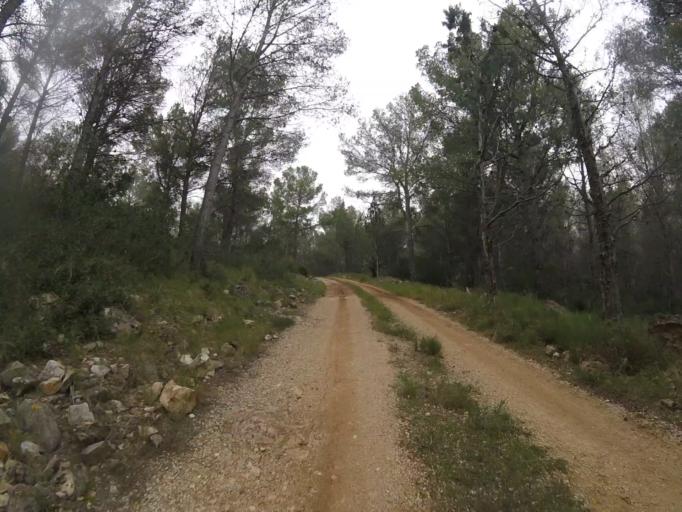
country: ES
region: Valencia
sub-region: Provincia de Castello
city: Santa Magdalena de Pulpis
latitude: 40.3186
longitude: 0.2780
